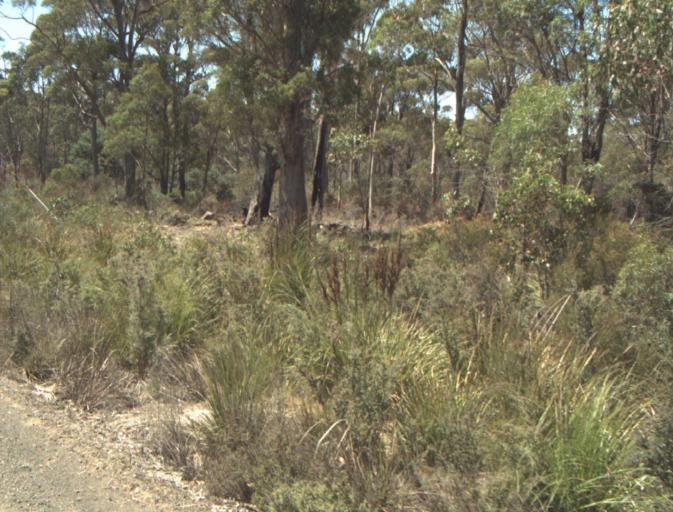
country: AU
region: Tasmania
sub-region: Launceston
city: Mayfield
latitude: -41.2781
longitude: 147.0977
